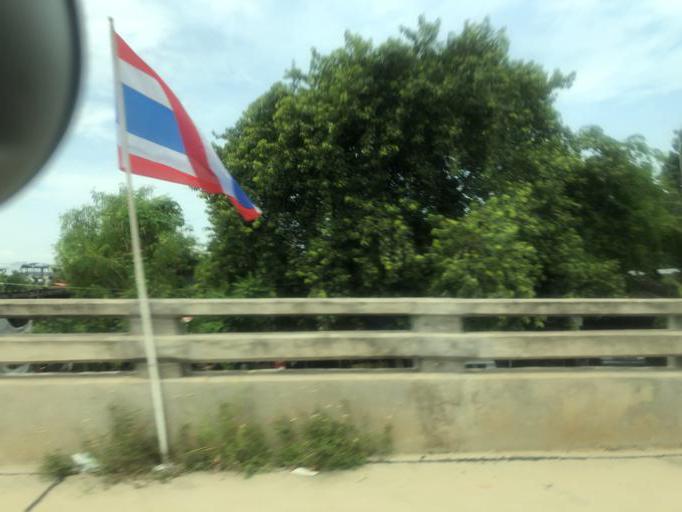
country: TH
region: Bangkok
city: Don Mueang
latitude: 13.9672
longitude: 100.6041
